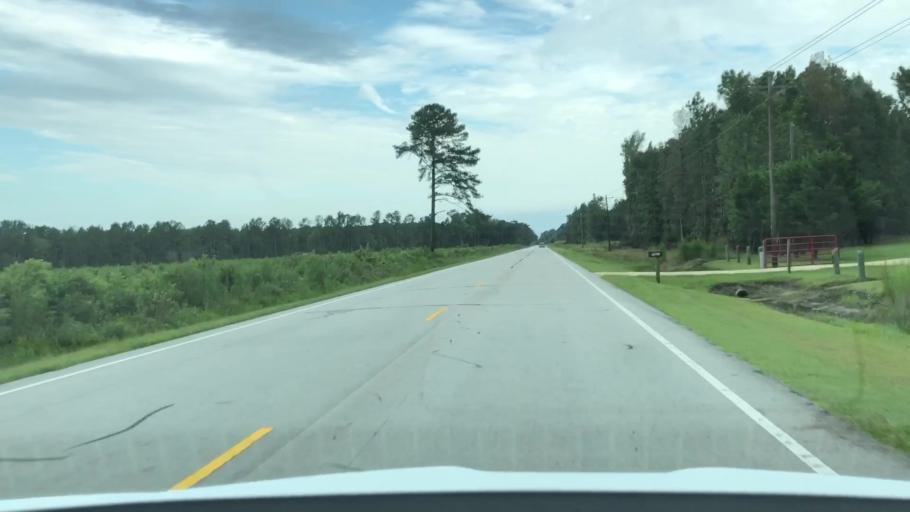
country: US
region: North Carolina
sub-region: Lenoir County
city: Kinston
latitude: 35.1275
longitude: -77.5218
